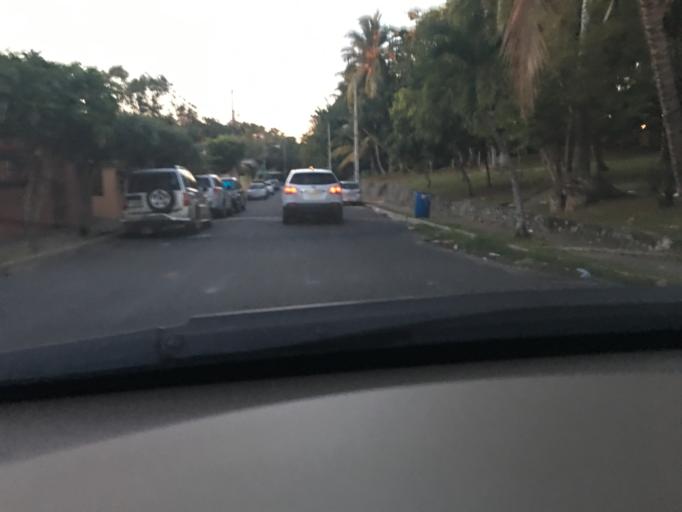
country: DO
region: Nacional
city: La Agustina
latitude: 18.4852
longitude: -69.9539
